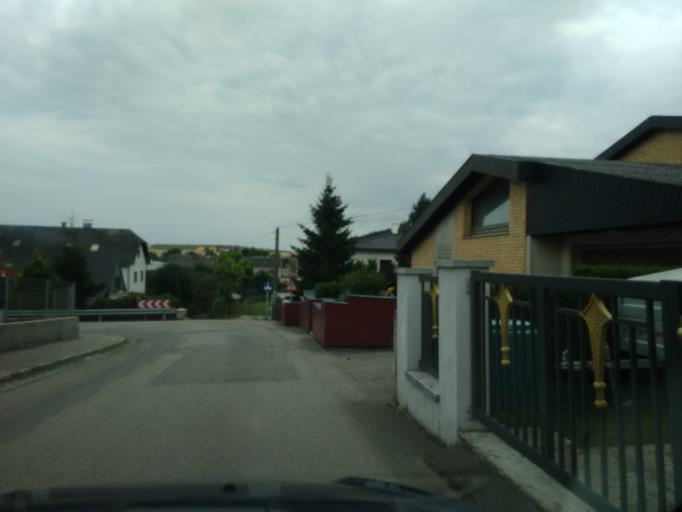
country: AT
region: Upper Austria
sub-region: Politischer Bezirk Grieskirchen
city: Bad Schallerbach
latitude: 48.2030
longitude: 13.9541
